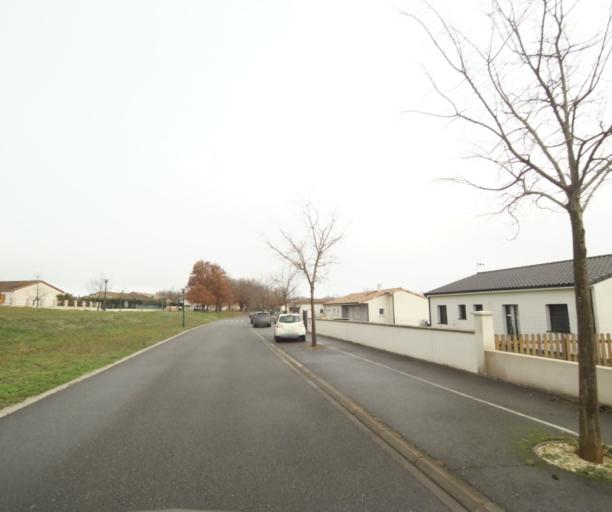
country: FR
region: Midi-Pyrenees
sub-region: Departement de la Haute-Garonne
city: Villemur-sur-Tarn
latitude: 43.8543
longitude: 1.4813
